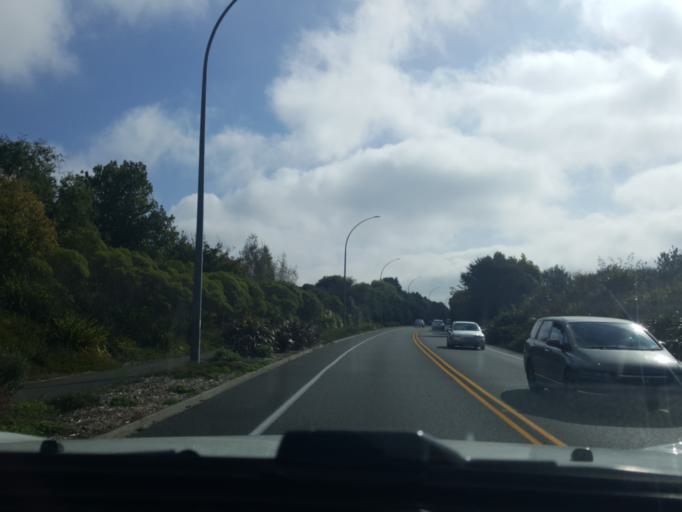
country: NZ
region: Waikato
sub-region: Hamilton City
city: Hamilton
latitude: -37.7426
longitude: 175.2664
